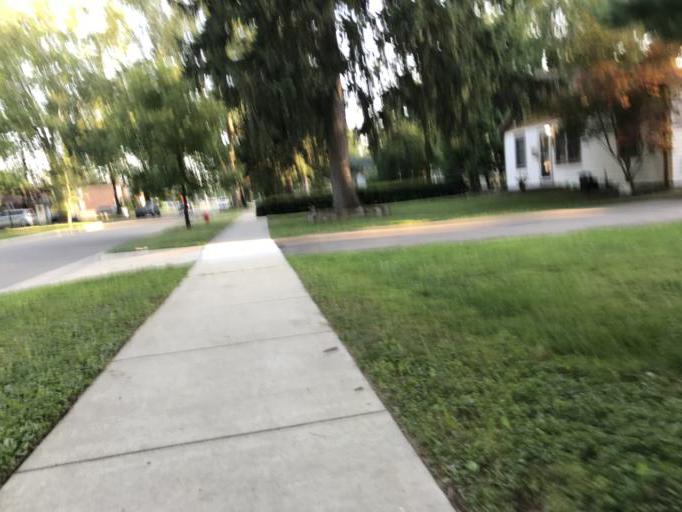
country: US
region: Michigan
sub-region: Oakland County
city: Farmington
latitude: 42.4612
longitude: -83.3520
